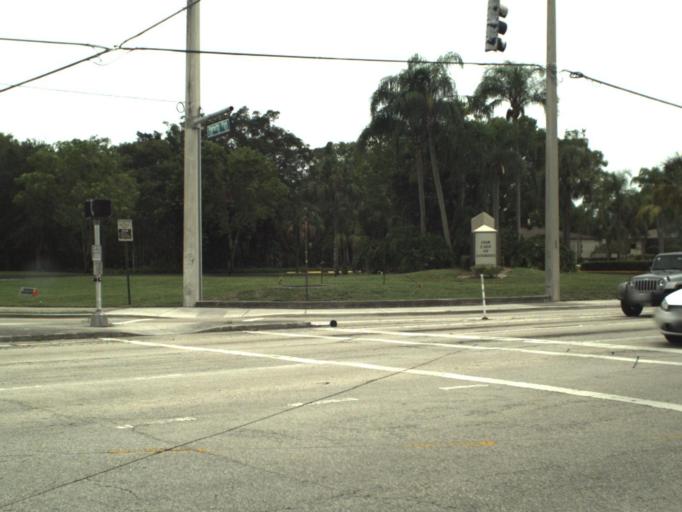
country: US
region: Florida
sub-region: Palm Beach County
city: Boca Pointe
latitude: 26.3493
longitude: -80.1866
